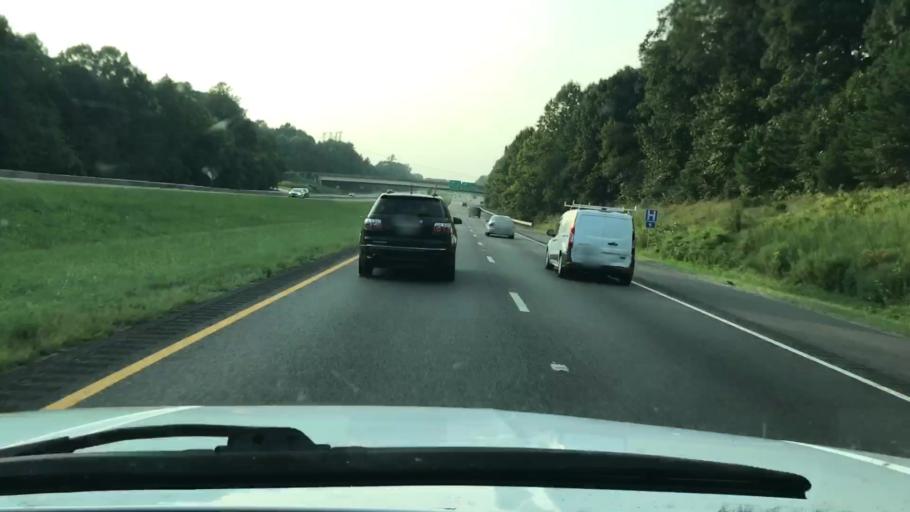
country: US
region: Virginia
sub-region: Chesterfield County
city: Brandermill
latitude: 37.4138
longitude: -77.6193
